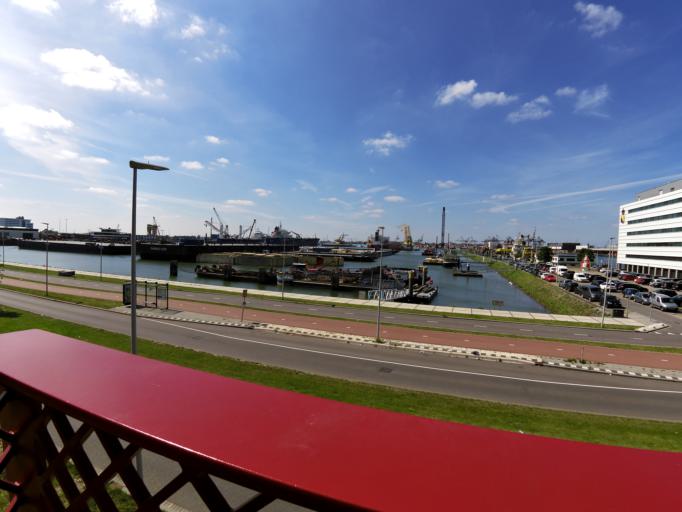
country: NL
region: South Holland
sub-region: Gemeente Rotterdam
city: Delfshaven
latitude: 51.8851
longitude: 4.4574
